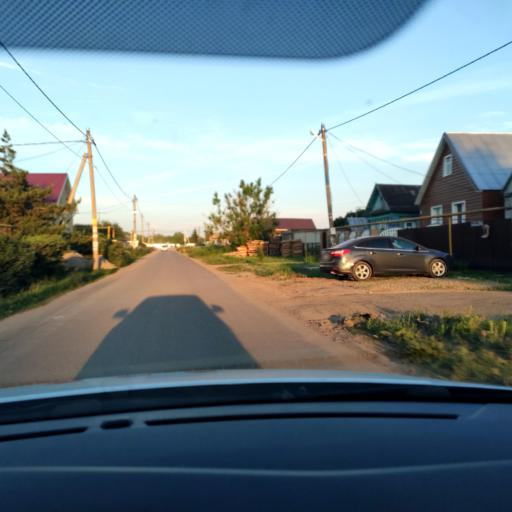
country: RU
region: Tatarstan
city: Stolbishchi
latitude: 55.7478
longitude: 49.3036
